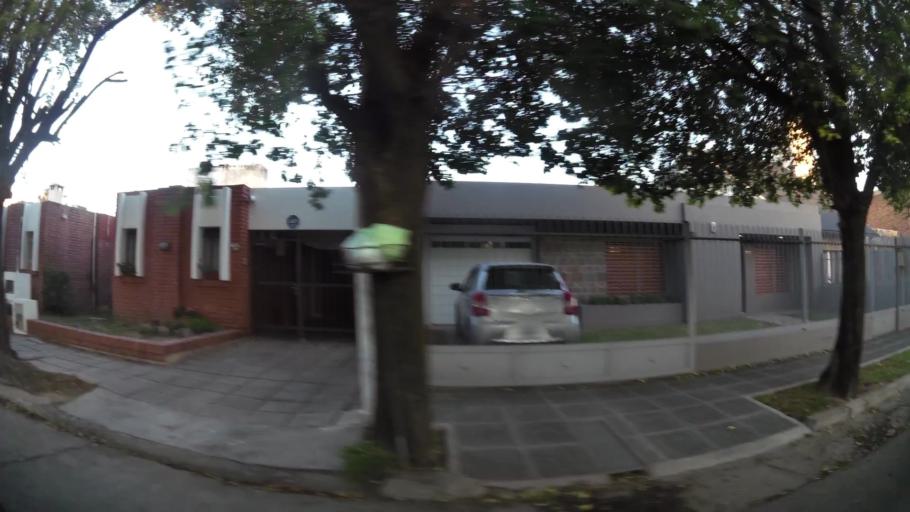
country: AR
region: Cordoba
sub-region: Departamento de Capital
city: Cordoba
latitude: -31.3770
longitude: -64.2212
